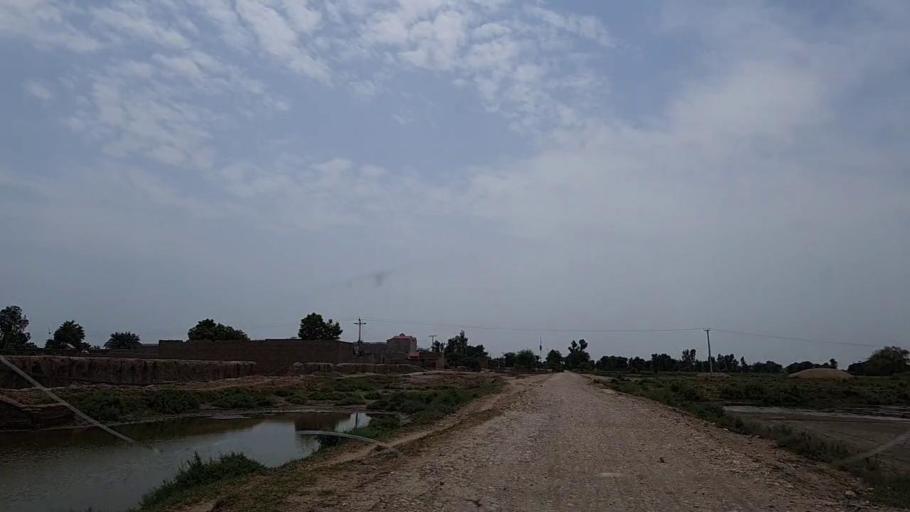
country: PK
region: Sindh
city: Tharu Shah
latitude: 26.9268
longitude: 68.0857
